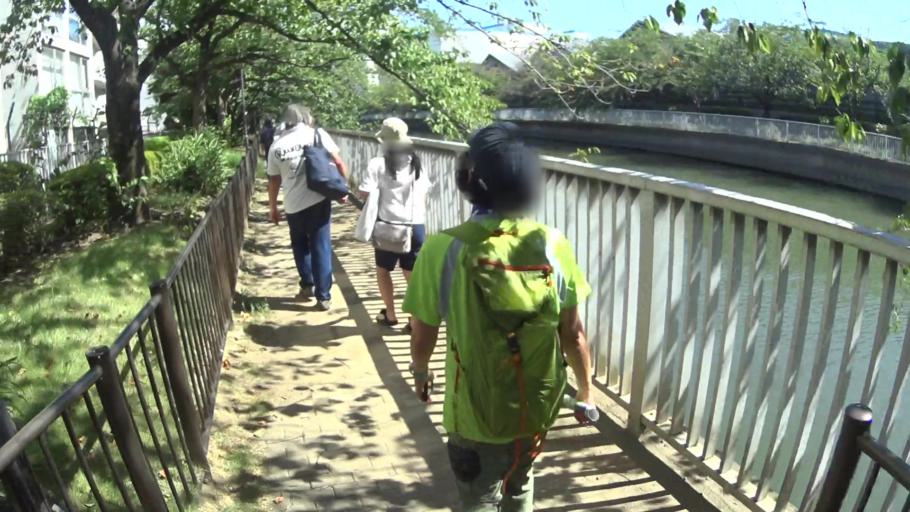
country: JP
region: Tokyo
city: Urayasu
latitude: 35.6723
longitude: 139.7919
